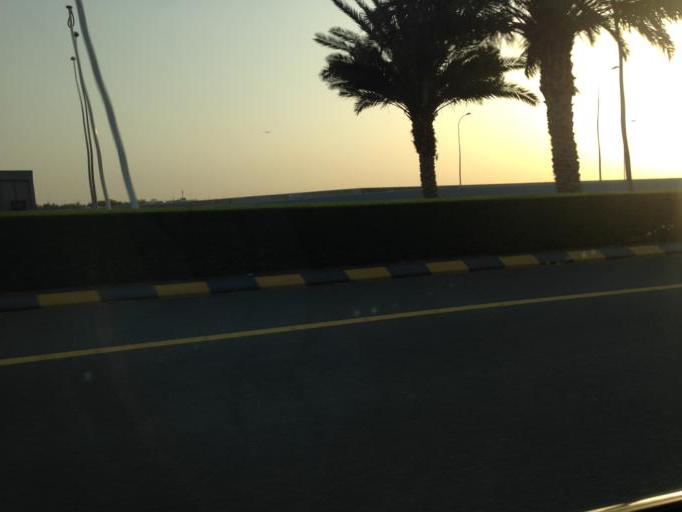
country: OM
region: Muhafazat Masqat
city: Bawshar
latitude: 23.5996
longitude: 58.3278
